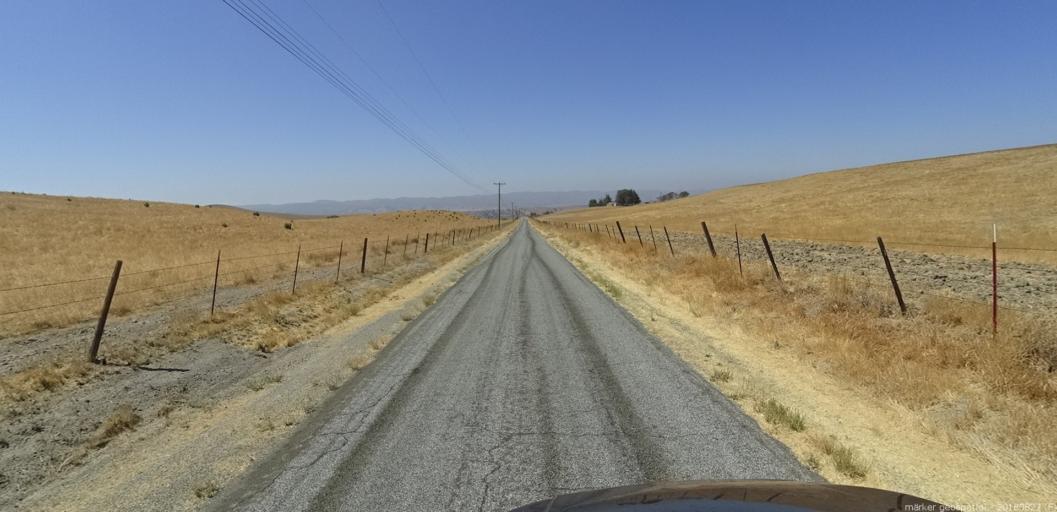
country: US
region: California
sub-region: Monterey County
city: King City
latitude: 36.0802
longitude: -120.9151
